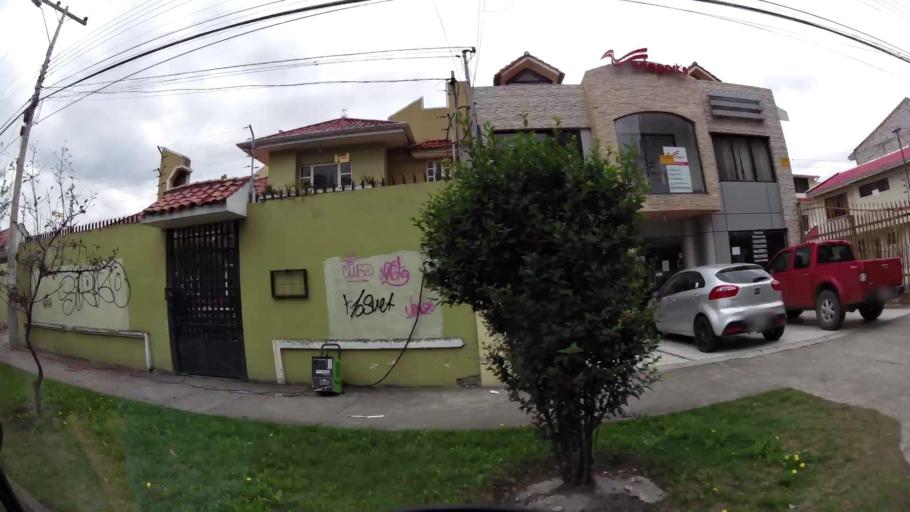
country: EC
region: Azuay
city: Cuenca
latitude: -2.9089
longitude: -79.0203
